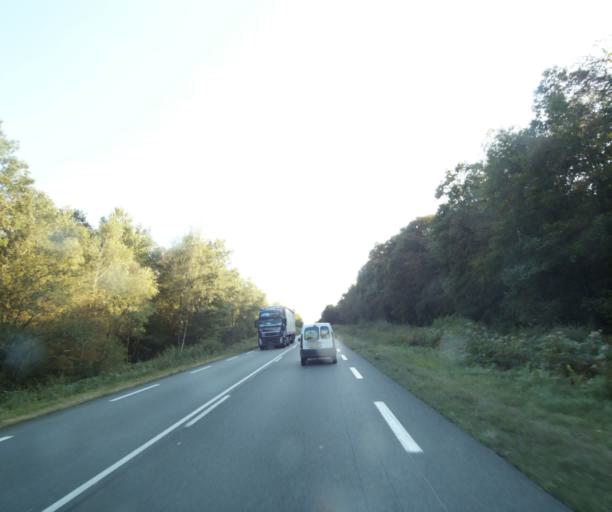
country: FR
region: Bourgogne
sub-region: Departement de Saone-et-Loire
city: Palinges
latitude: 46.5399
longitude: 4.1718
